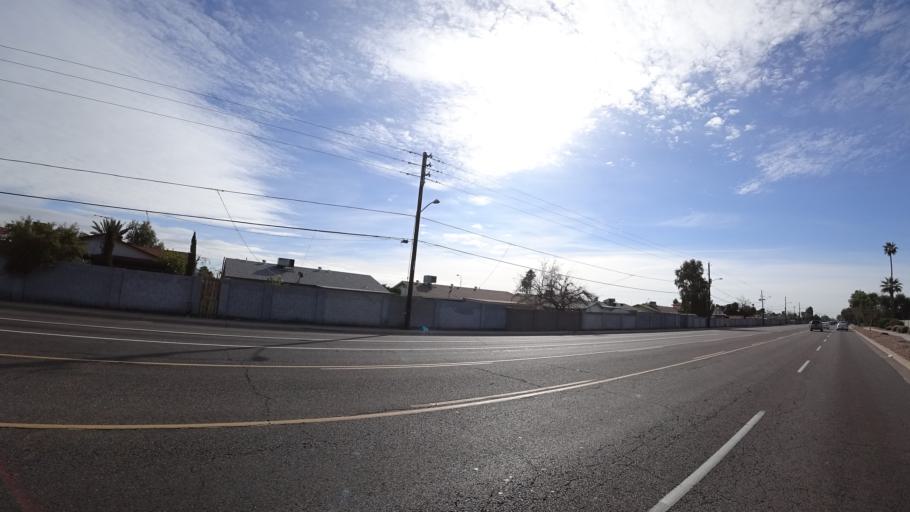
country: US
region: Arizona
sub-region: Maricopa County
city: Glendale
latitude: 33.5597
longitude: -112.1517
